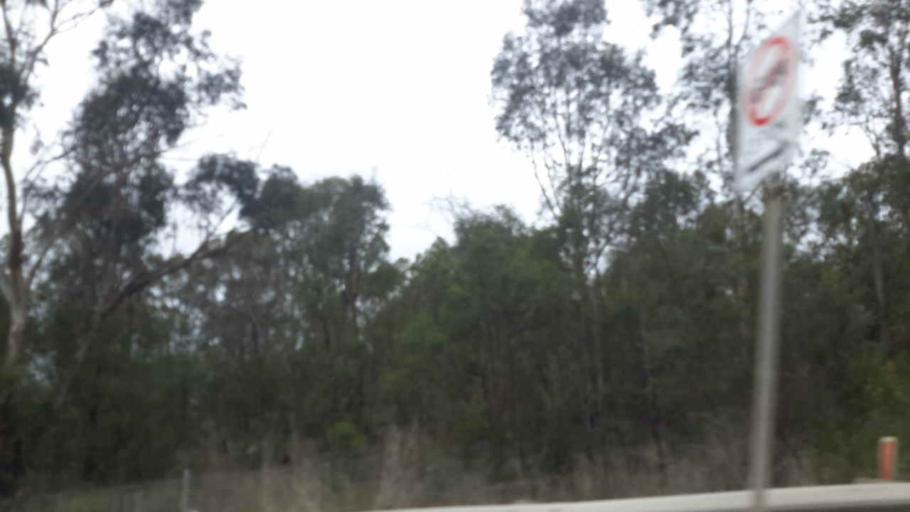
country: AU
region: New South Wales
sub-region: Hawkesbury
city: South Windsor
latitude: -33.6375
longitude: 150.7822
